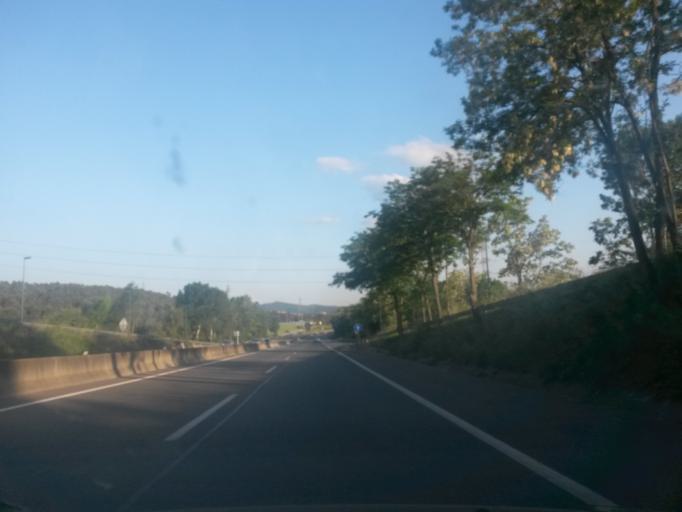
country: ES
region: Catalonia
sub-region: Provincia de Girona
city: Palol de Revardit
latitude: 42.0571
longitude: 2.8152
